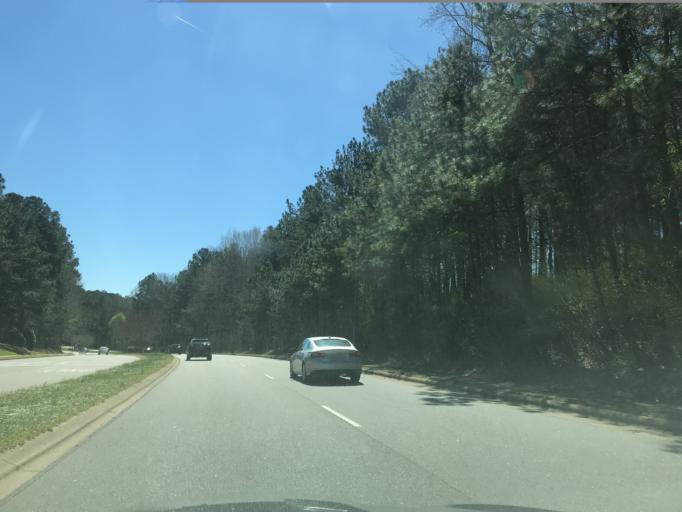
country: US
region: North Carolina
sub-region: Wake County
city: Garner
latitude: 35.6887
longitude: -78.6334
